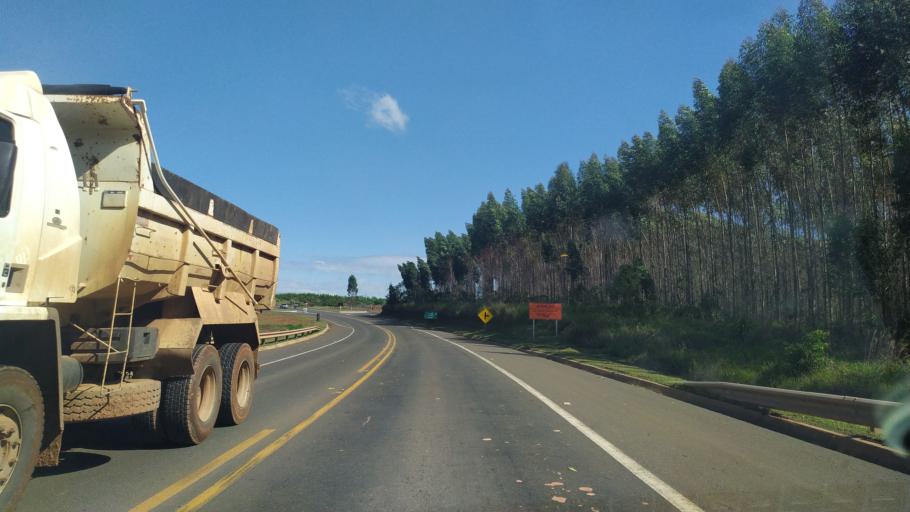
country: BR
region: Parana
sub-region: Telemaco Borba
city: Telemaco Borba
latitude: -24.2441
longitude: -50.7739
